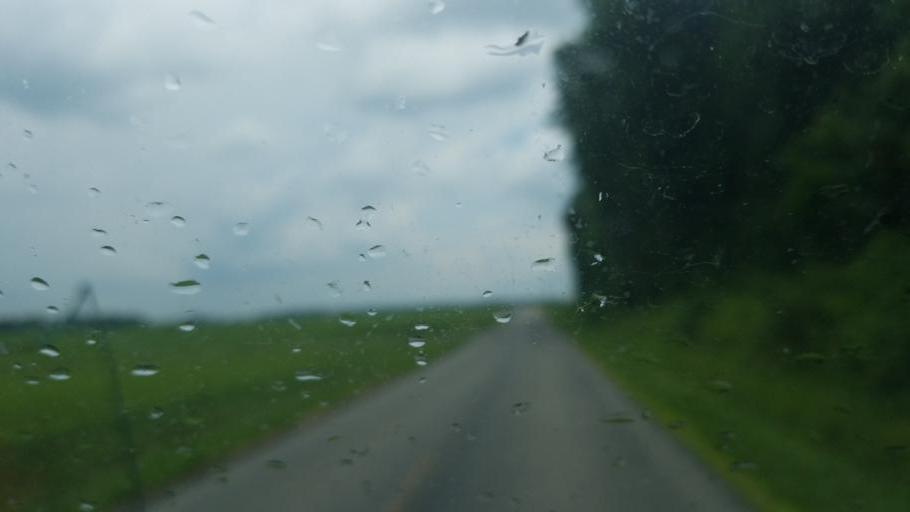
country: US
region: Ohio
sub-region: Wayne County
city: West Salem
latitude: 40.8579
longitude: -82.0873
